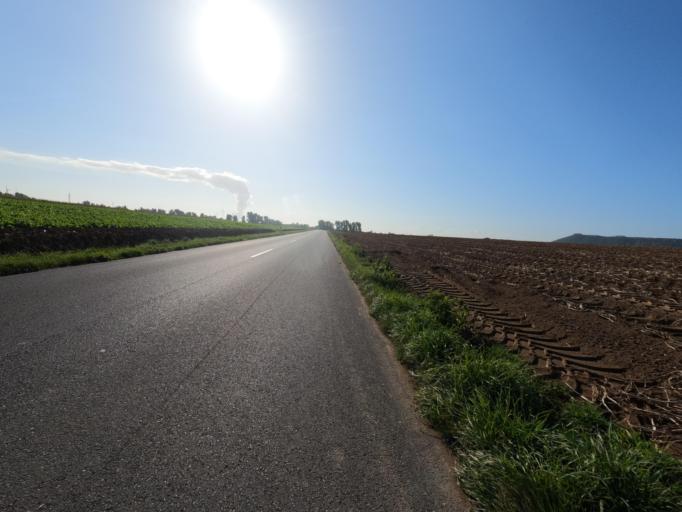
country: DE
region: North Rhine-Westphalia
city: Siersdorf
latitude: 50.9389
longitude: 6.2481
